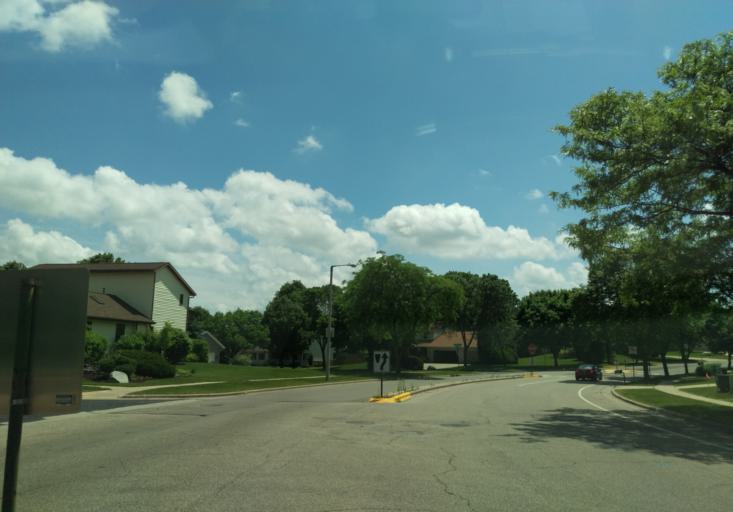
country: US
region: Wisconsin
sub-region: Dane County
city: Middleton
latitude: 43.0887
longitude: -89.5183
